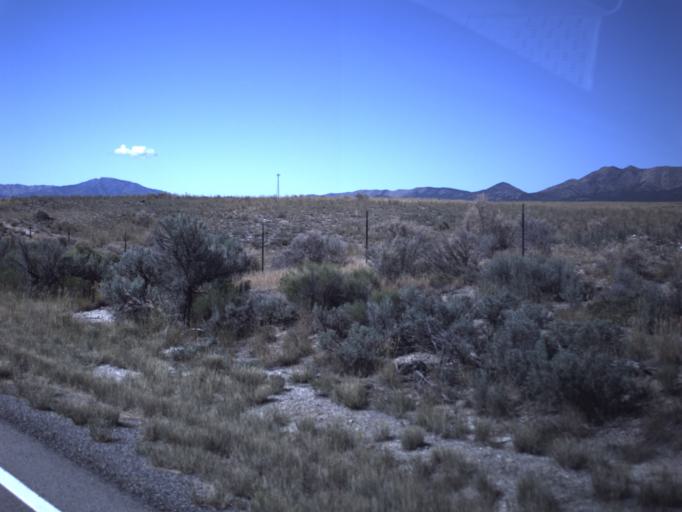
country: US
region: Utah
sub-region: Tooele County
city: Tooele
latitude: 40.2105
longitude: -112.4077
